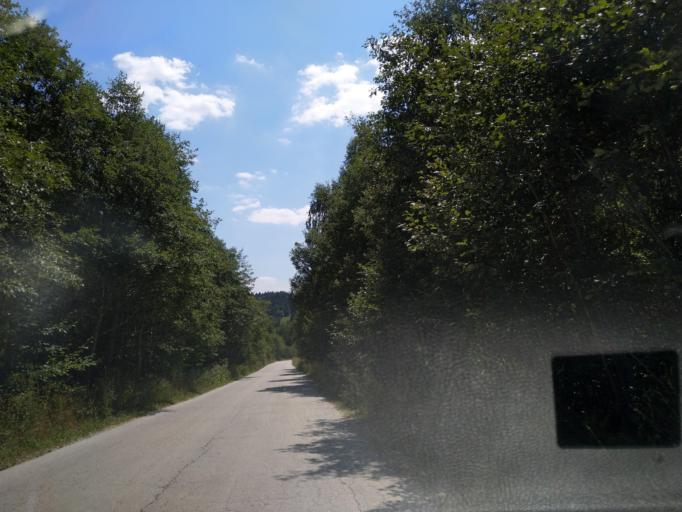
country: RS
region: Central Serbia
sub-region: Zlatiborski Okrug
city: Nova Varos
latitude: 43.4623
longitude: 19.9754
